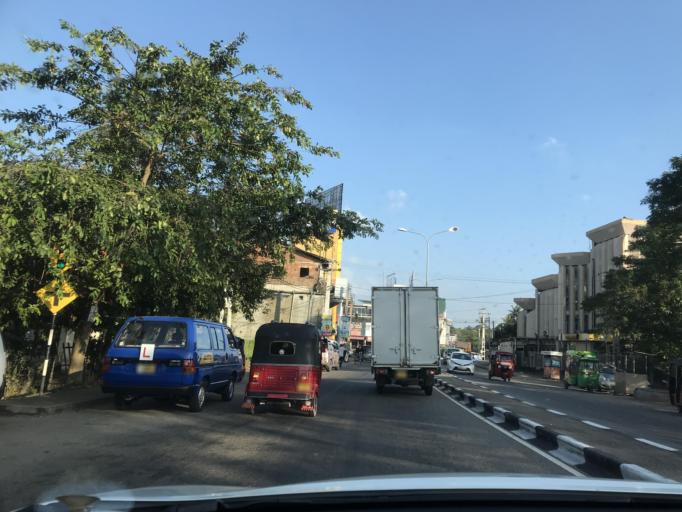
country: LK
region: Western
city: Ja Ela
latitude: 7.0822
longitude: 79.8901
